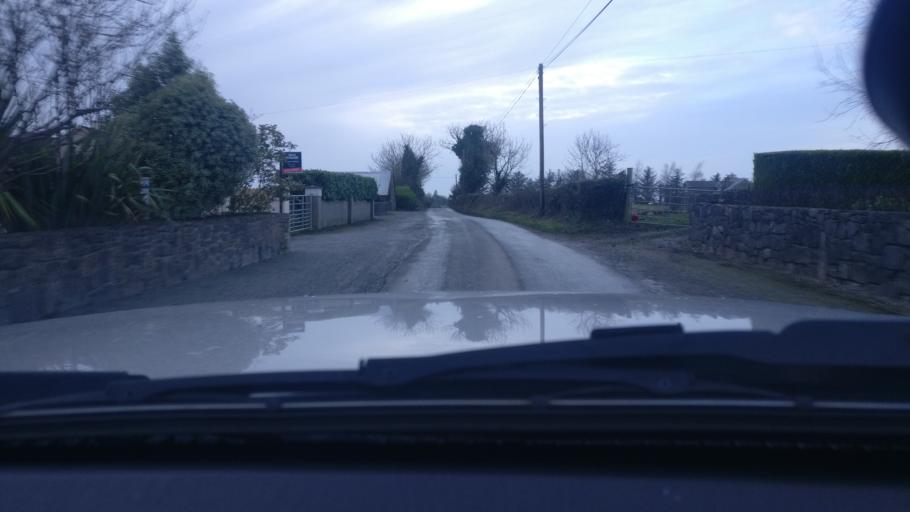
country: IE
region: Connaught
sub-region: County Galway
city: Loughrea
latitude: 53.1640
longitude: -8.5435
